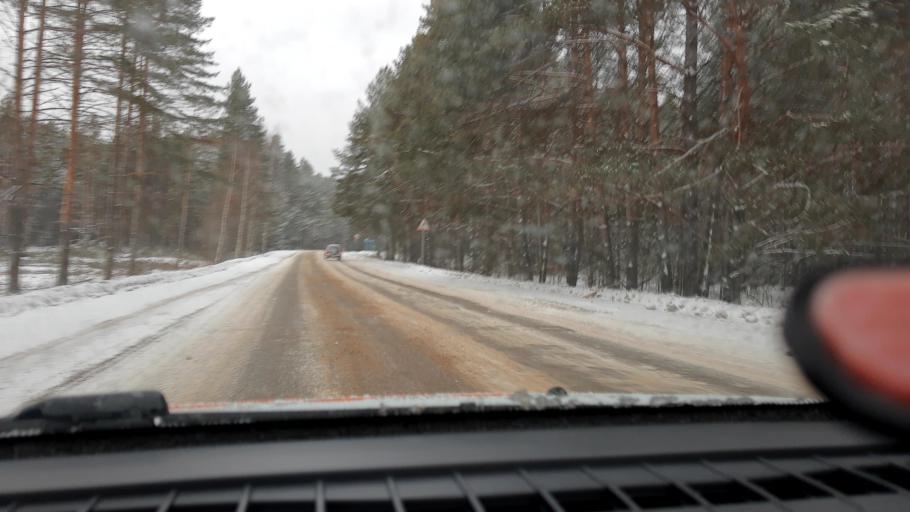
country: RU
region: Nizjnij Novgorod
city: Pamyat' Parizhskoy Kommuny
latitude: 56.2773
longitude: 44.3911
